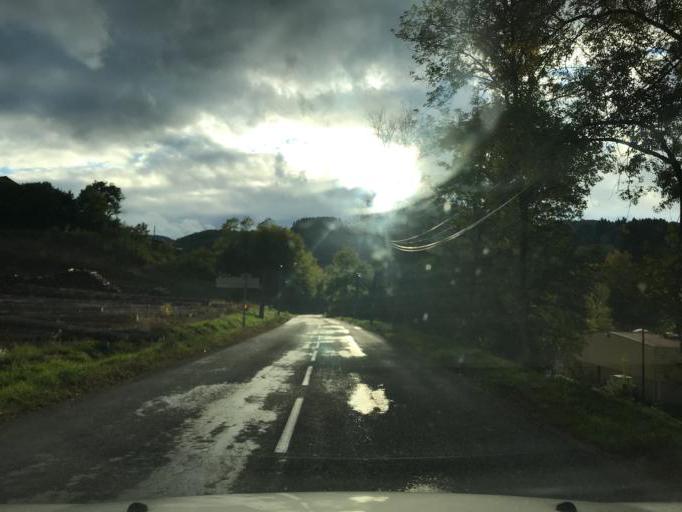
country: FR
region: Rhone-Alpes
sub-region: Departement du Rhone
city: Grandris
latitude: 46.0231
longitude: 4.5035
